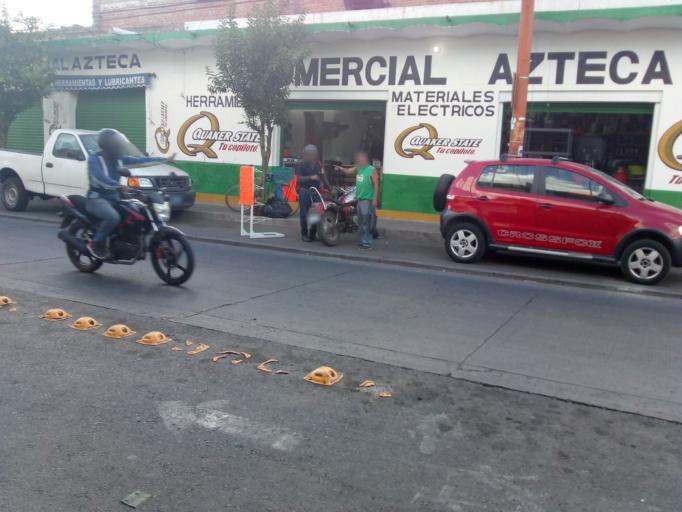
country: MX
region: Guanajuato
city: Leon
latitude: 21.1388
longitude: -101.6822
